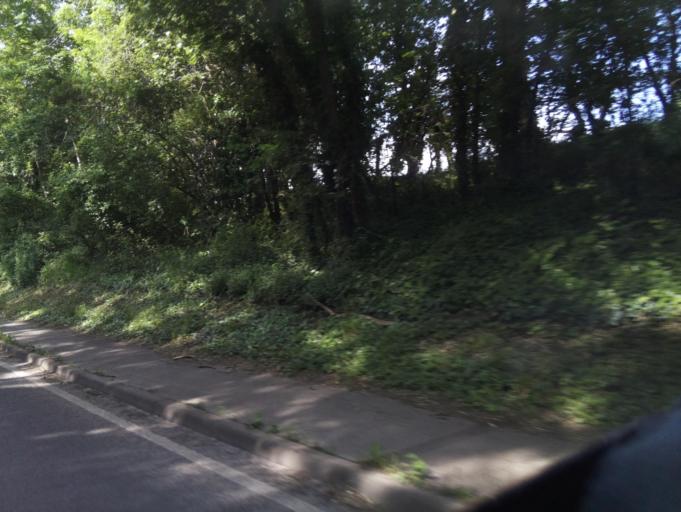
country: GB
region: England
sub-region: Worcestershire
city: Pershore
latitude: 52.1281
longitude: -2.1051
